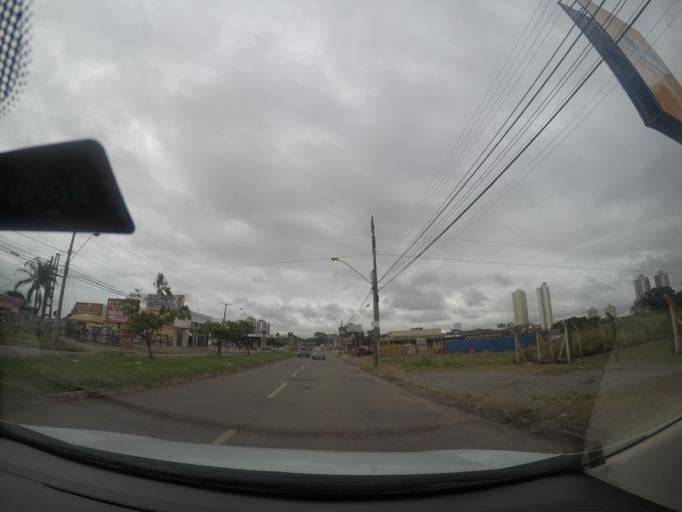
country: BR
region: Goias
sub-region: Goiania
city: Goiania
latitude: -16.7468
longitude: -49.2858
